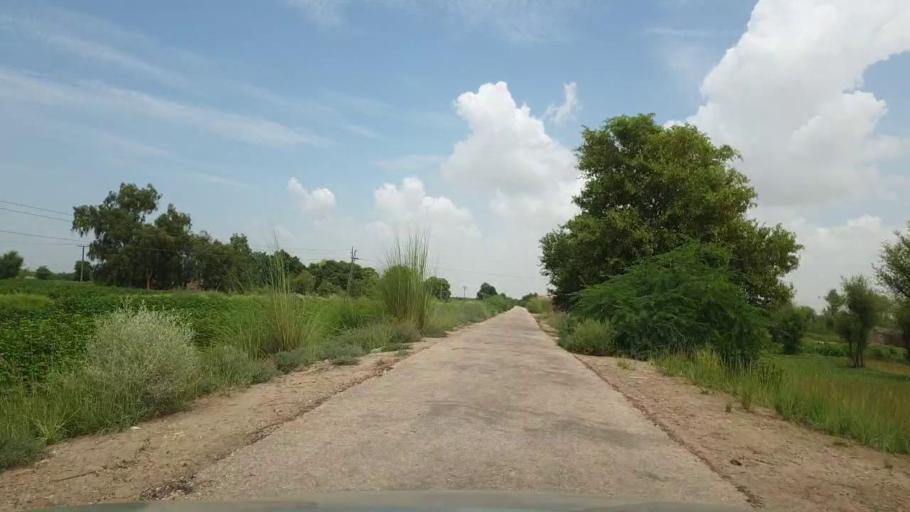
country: PK
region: Sindh
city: Bozdar
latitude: 27.0229
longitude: 68.9485
